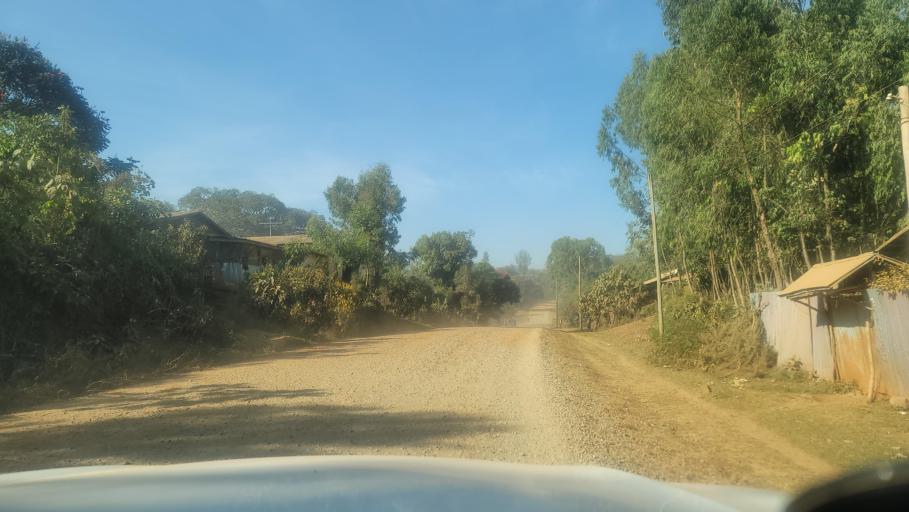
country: ET
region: Oromiya
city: Agaro
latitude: 7.8396
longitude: 36.5579
